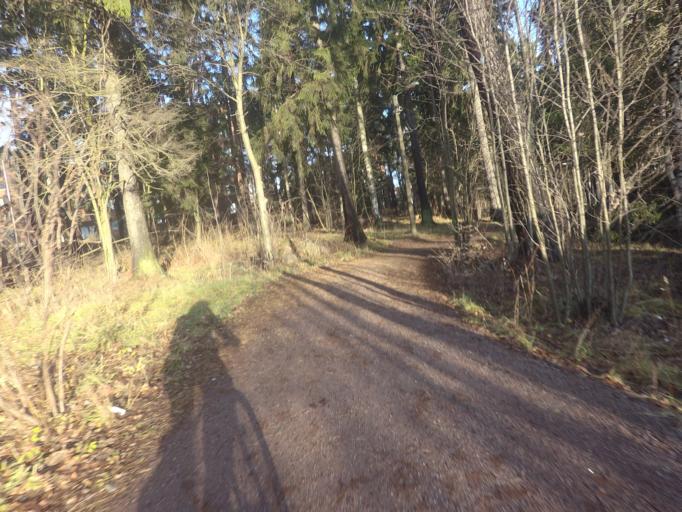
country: FI
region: Uusimaa
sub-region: Helsinki
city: Teekkarikylae
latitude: 60.1866
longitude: 24.8371
